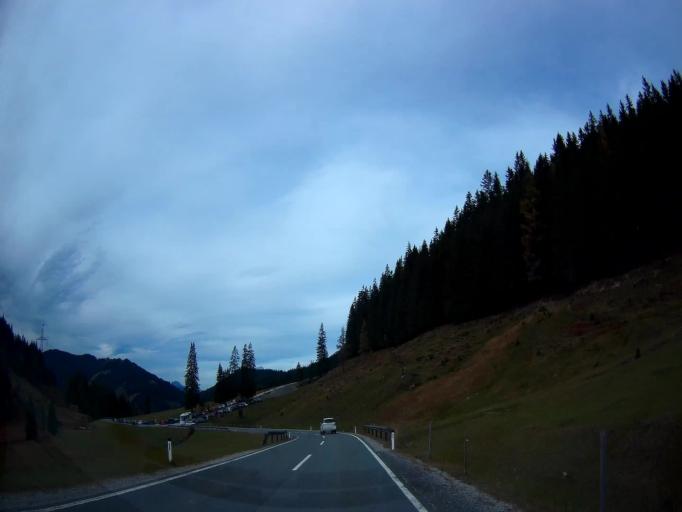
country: AT
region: Salzburg
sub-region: Politischer Bezirk Zell am See
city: Dienten am Hochkonig
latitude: 47.3913
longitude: 13.0512
